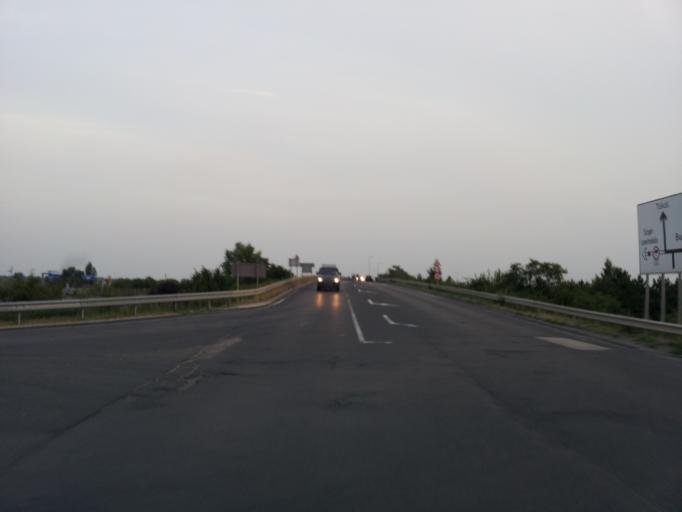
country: HU
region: Pest
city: Szigetszentmiklos
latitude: 47.3815
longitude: 19.0497
